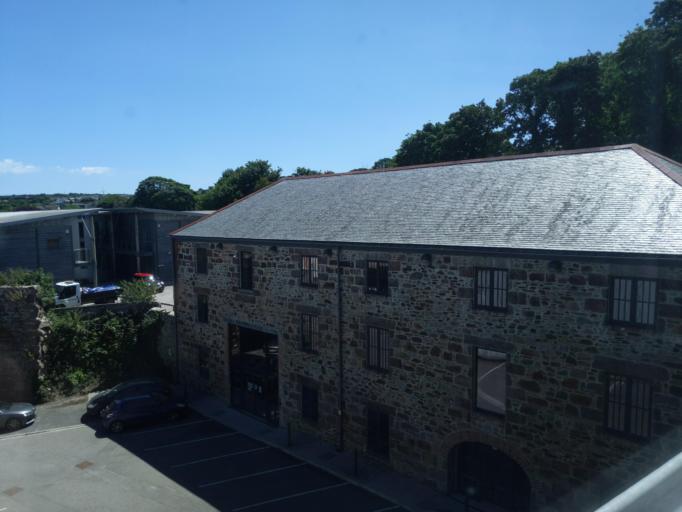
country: GB
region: England
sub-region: Cornwall
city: Hayle
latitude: 50.1840
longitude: -5.4229
